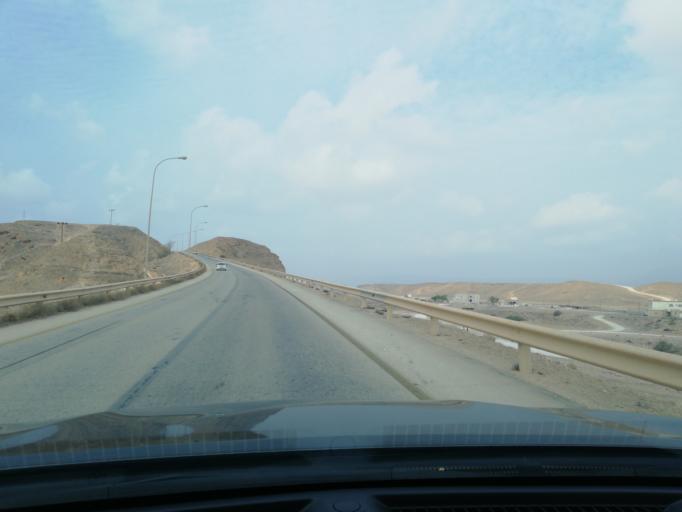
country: OM
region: Zufar
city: Salalah
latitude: 16.9555
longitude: 53.8639
